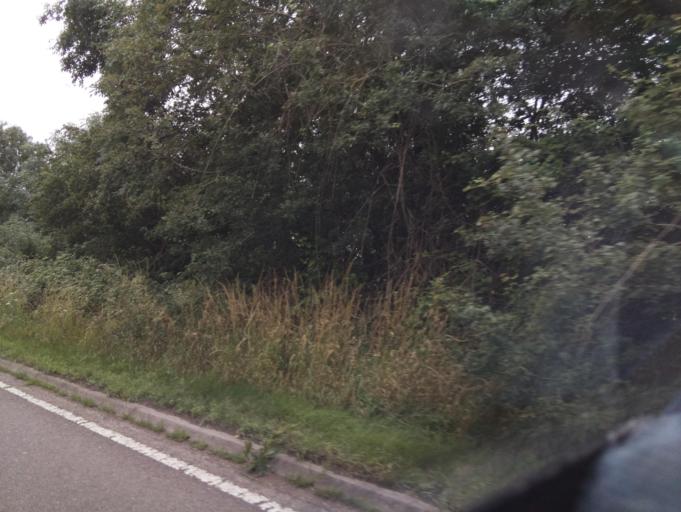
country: GB
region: England
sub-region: Northamptonshire
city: Corby
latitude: 52.4707
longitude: -0.7409
